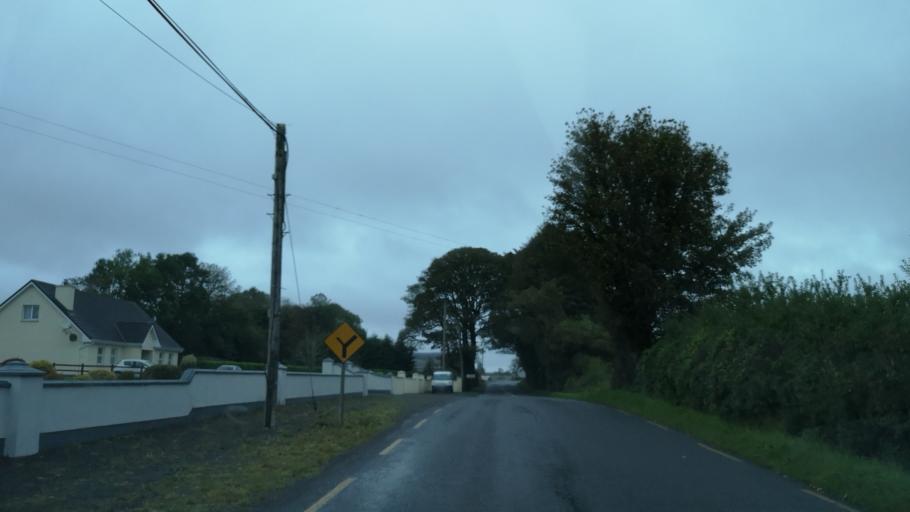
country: IE
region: Connaught
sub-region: Maigh Eo
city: Ballyhaunis
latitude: 53.8064
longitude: -8.6784
